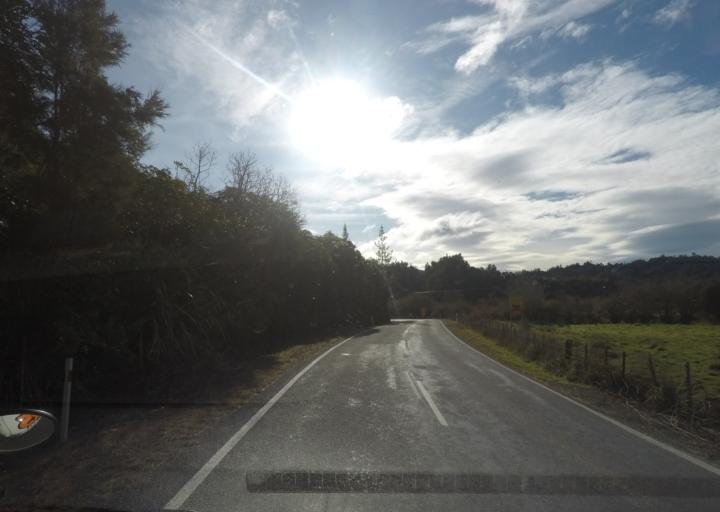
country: NZ
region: Tasman
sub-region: Tasman District
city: Motueka
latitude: -41.0187
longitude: 172.9807
